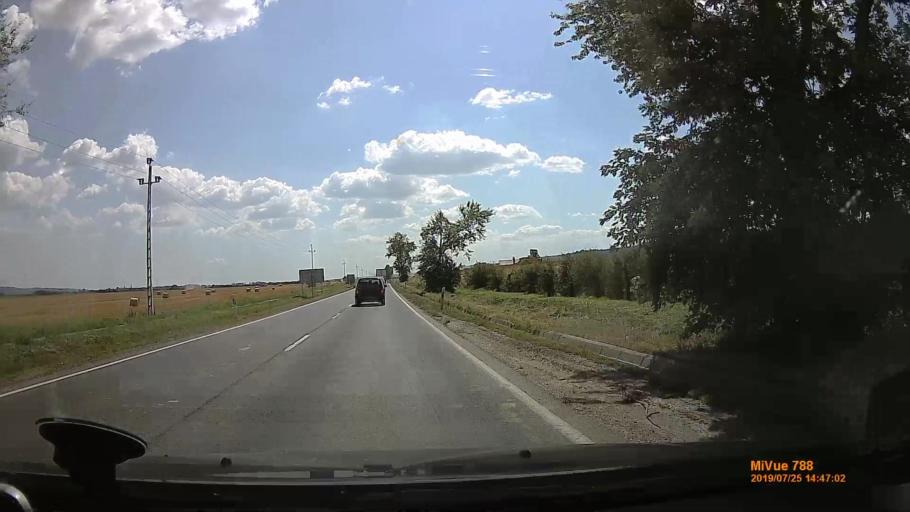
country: HU
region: Borsod-Abauj-Zemplen
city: Halmaj
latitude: 48.2506
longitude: 20.9782
